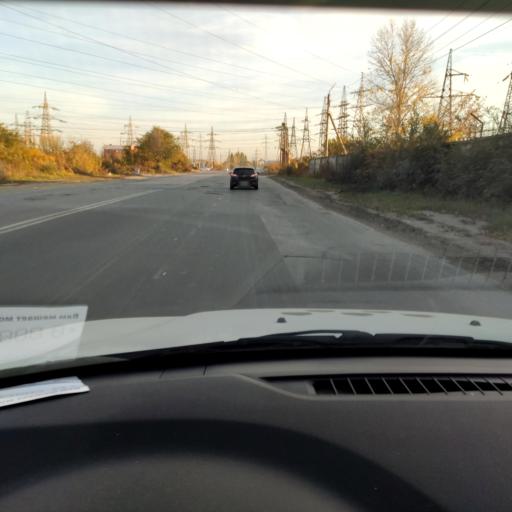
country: RU
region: Samara
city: Zhigulevsk
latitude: 53.5137
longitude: 49.4643
